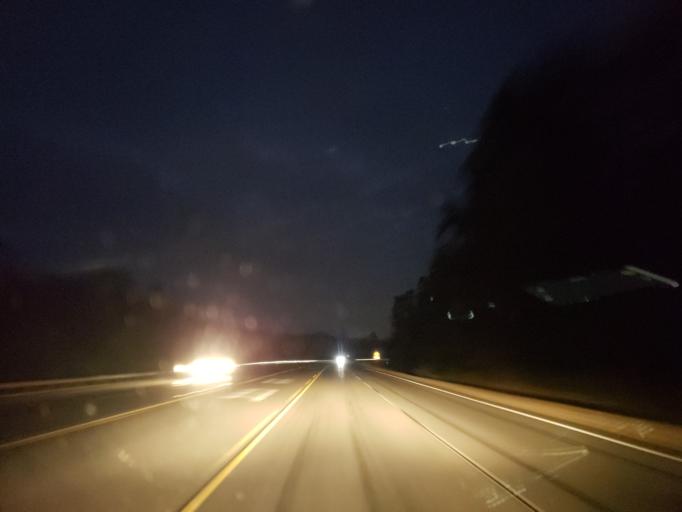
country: US
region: Georgia
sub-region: Polk County
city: Rockmart
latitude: 34.0326
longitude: -85.0138
